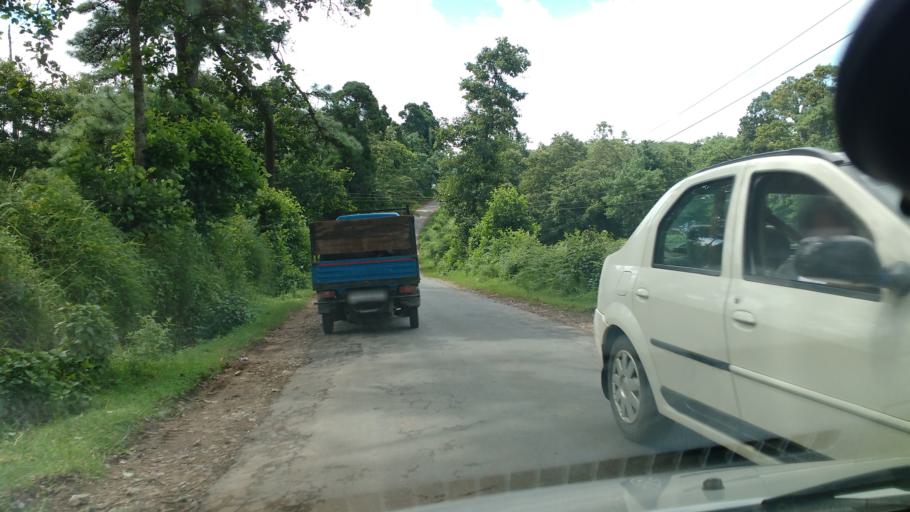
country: IN
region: Meghalaya
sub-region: East Khasi Hills
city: Shillong
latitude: 25.5434
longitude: 91.8473
